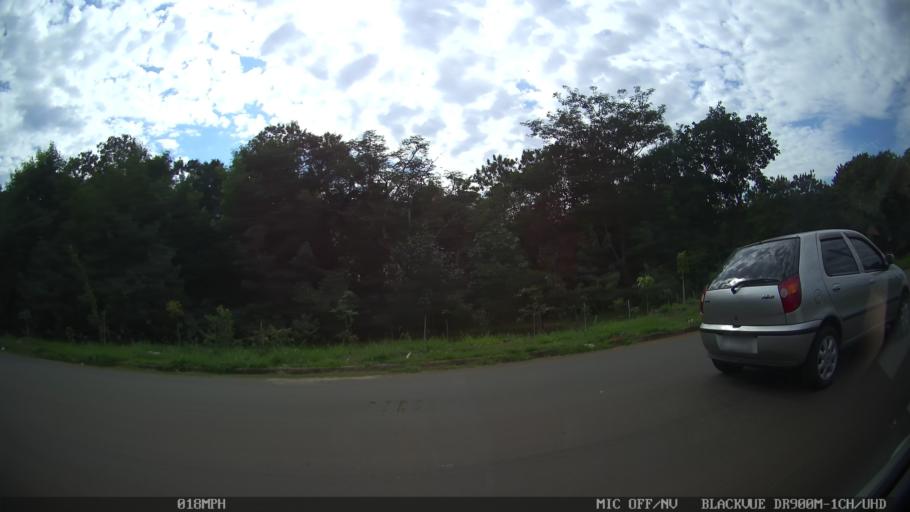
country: BR
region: Sao Paulo
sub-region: Americana
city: Americana
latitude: -22.7365
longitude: -47.3706
